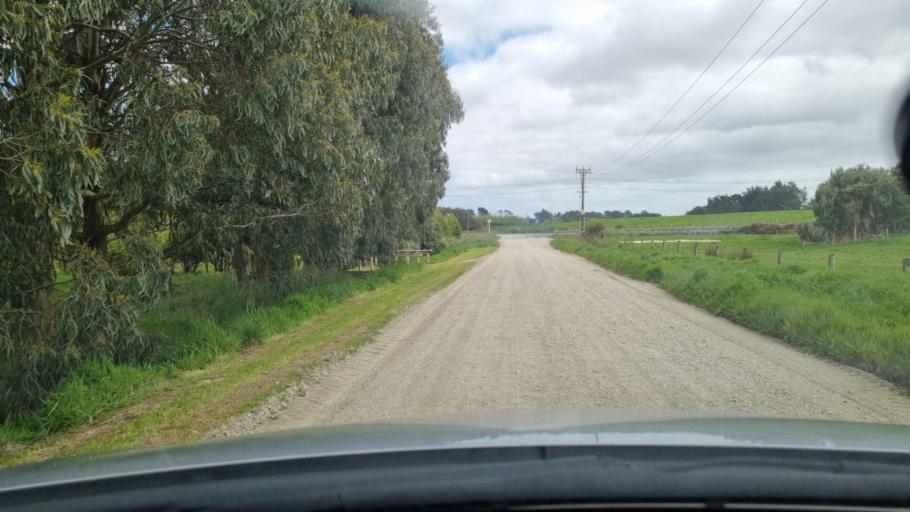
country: NZ
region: Southland
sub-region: Invercargill City
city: Invercargill
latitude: -46.4433
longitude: 168.4010
